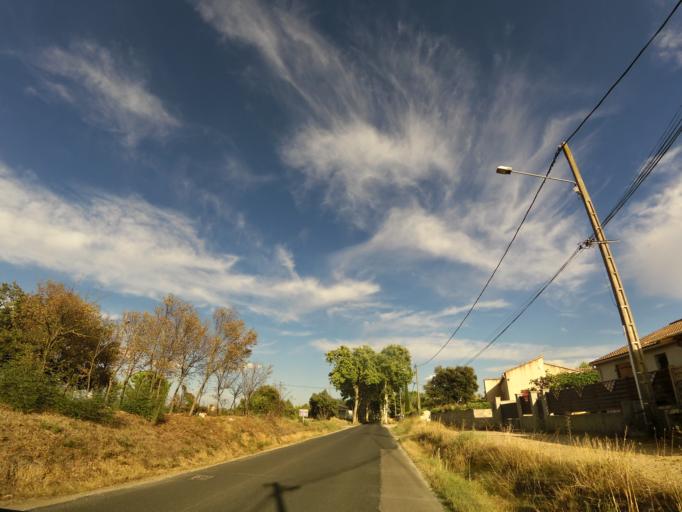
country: FR
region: Languedoc-Roussillon
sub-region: Departement de l'Herault
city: Beaulieu
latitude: 43.7714
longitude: 4.0112
